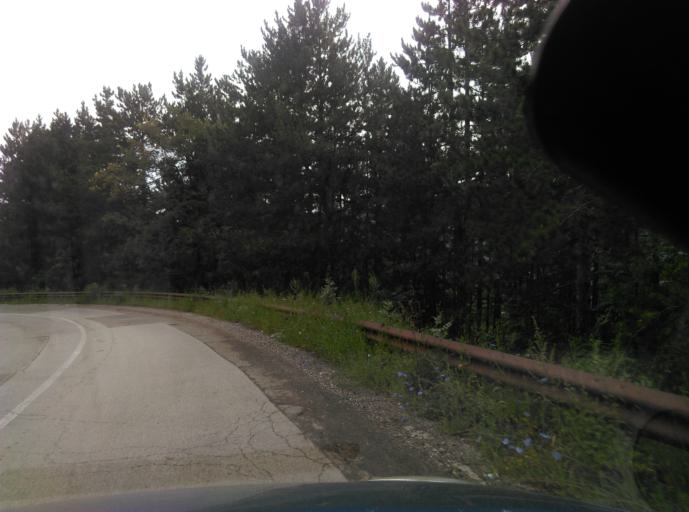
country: BG
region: Sofia-Capital
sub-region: Stolichna Obshtina
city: Sofia
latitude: 42.5908
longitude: 23.4064
